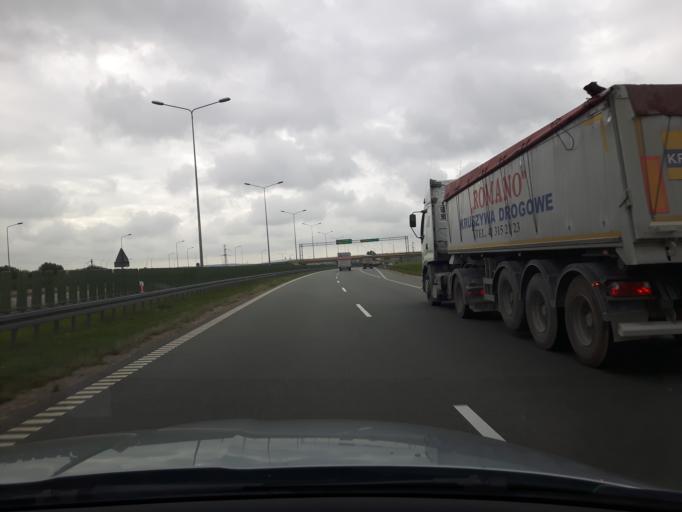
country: PL
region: Swietokrzyskie
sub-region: Powiat kielecki
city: Checiny
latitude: 50.8131
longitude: 20.4828
